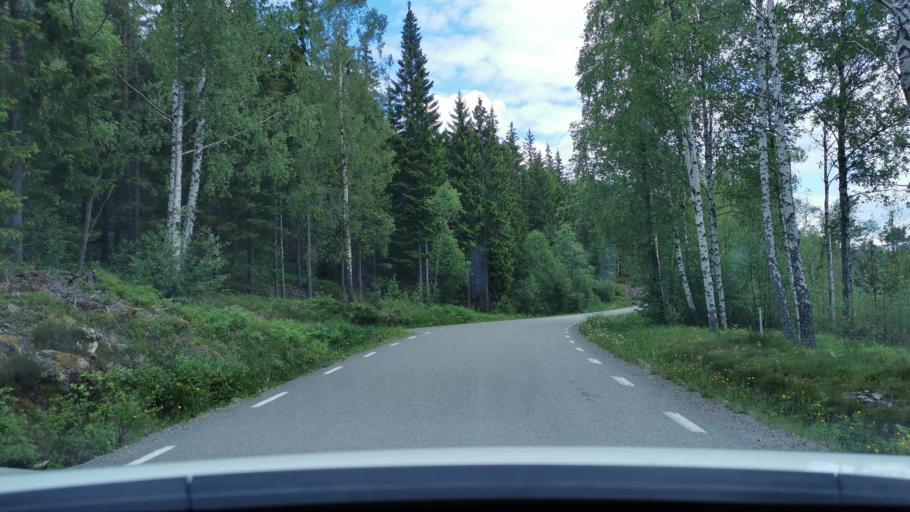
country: SE
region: Vaestra Goetaland
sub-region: Bengtsfors Kommun
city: Dals Langed
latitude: 58.8582
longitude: 12.3271
